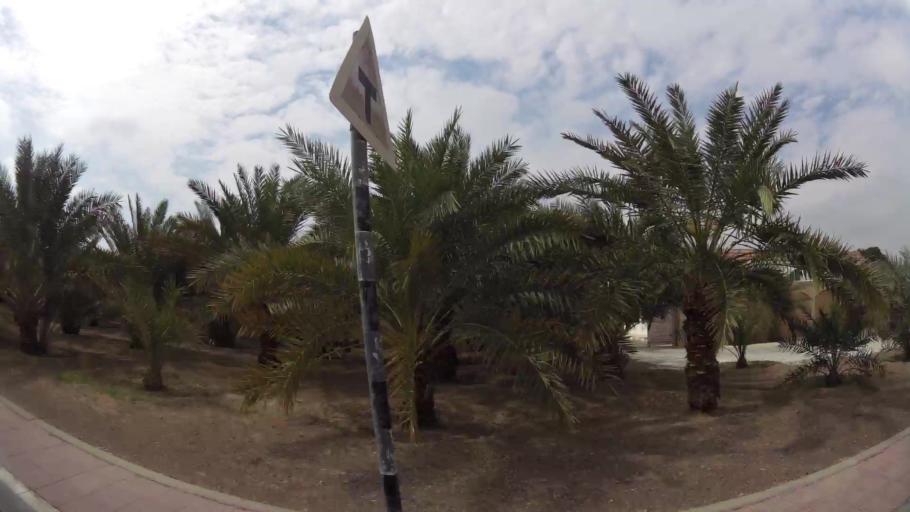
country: AE
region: Abu Dhabi
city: Al Ain
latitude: 24.2004
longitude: 55.7911
